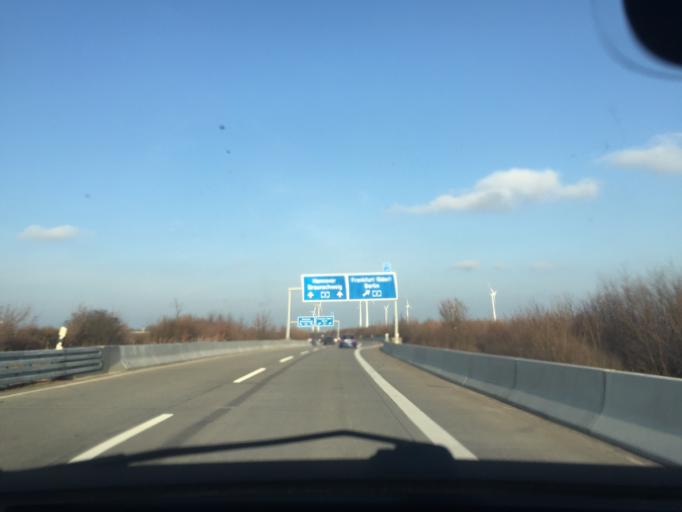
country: DE
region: Saxony-Anhalt
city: Dahlenwarsleben
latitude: 52.1622
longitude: 11.5451
